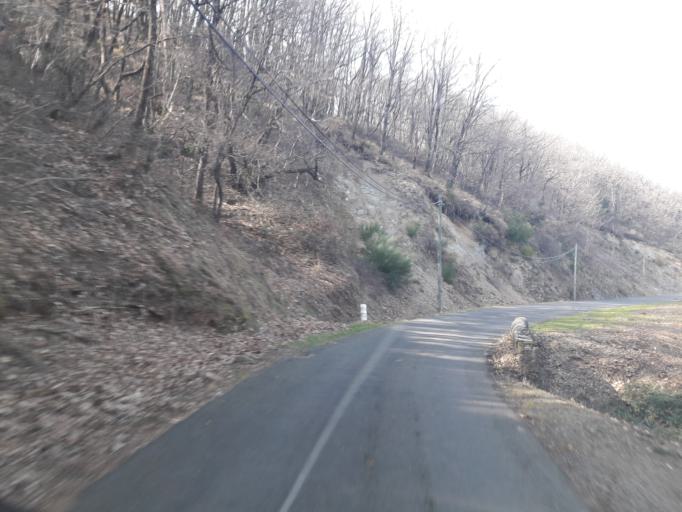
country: FR
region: Languedoc-Roussillon
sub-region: Departement du Gard
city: Sumene
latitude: 44.0069
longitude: 3.7786
